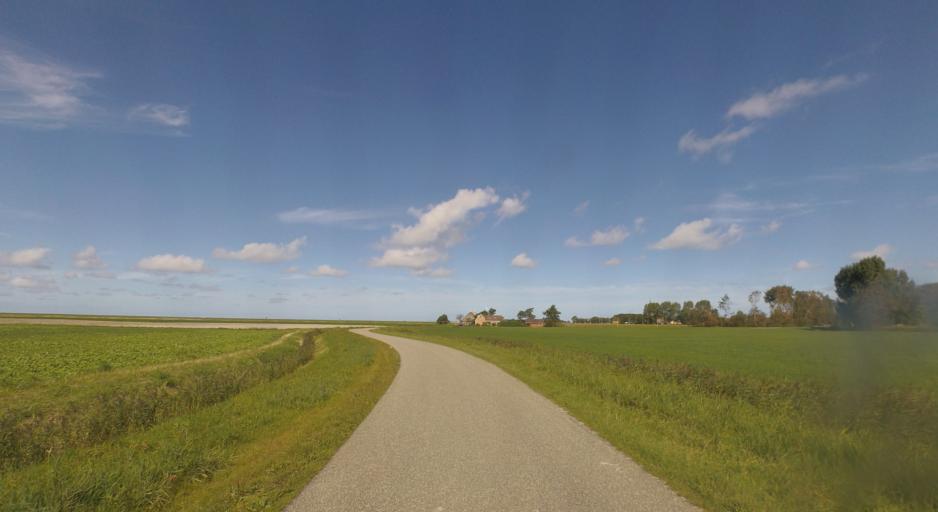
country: NL
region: Friesland
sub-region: Gemeente Dongeradeel
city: Holwerd
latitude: 53.3634
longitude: 5.8951
